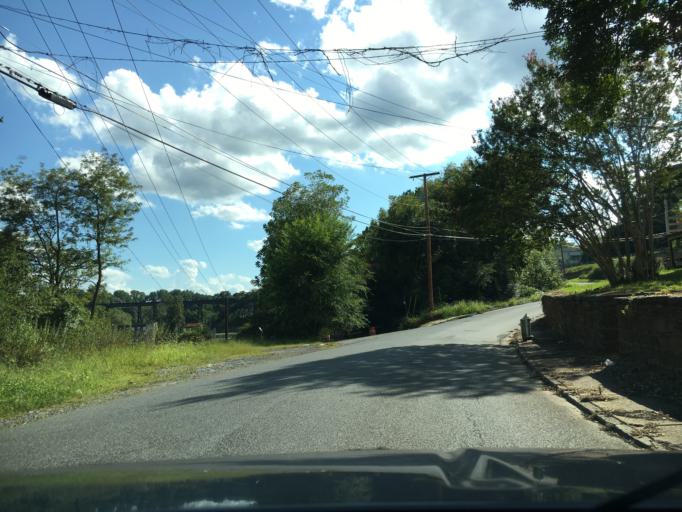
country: US
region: Virginia
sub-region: City of Lynchburg
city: Lynchburg
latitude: 37.3962
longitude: -79.1553
